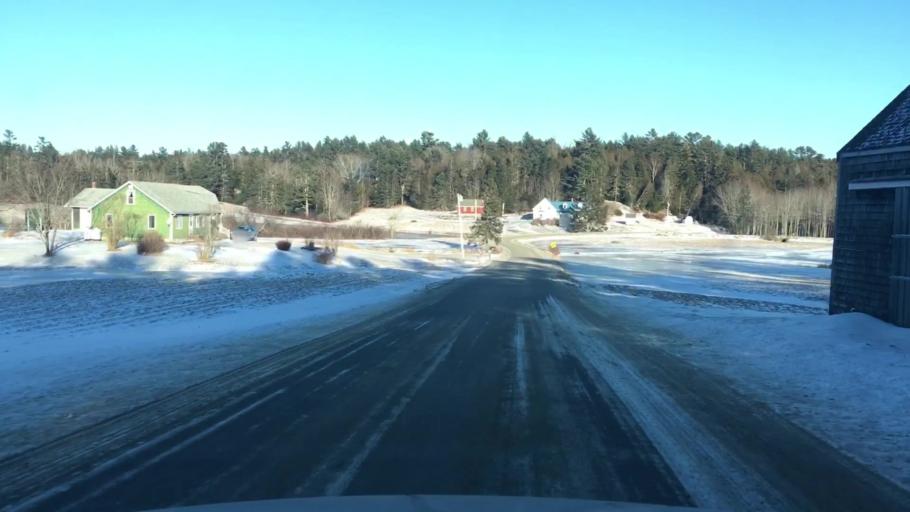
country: US
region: Maine
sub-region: Hancock County
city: Castine
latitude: 44.3859
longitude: -68.7415
